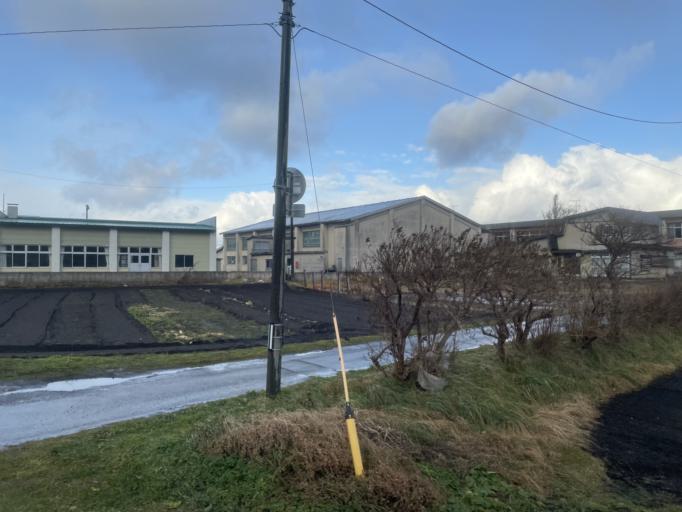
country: JP
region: Aomori
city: Misawa
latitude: 40.9171
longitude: 141.1919
